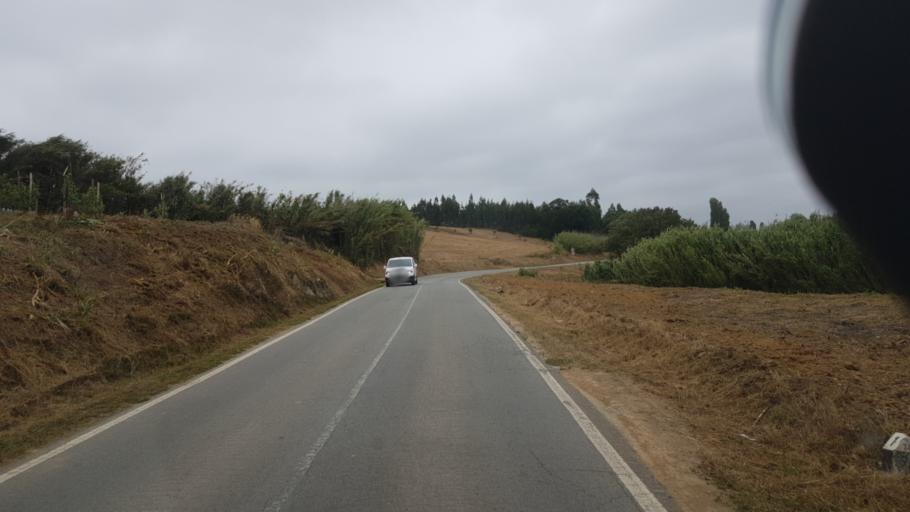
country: PT
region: Leiria
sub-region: Bombarral
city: Bombarral
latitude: 39.2899
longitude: -9.1992
